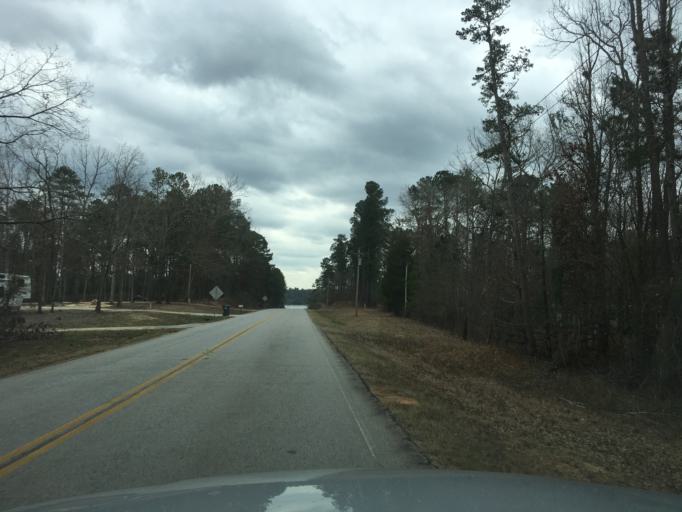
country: US
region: Georgia
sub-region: Lincoln County
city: Lincolnton
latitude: 33.8339
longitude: -82.4096
